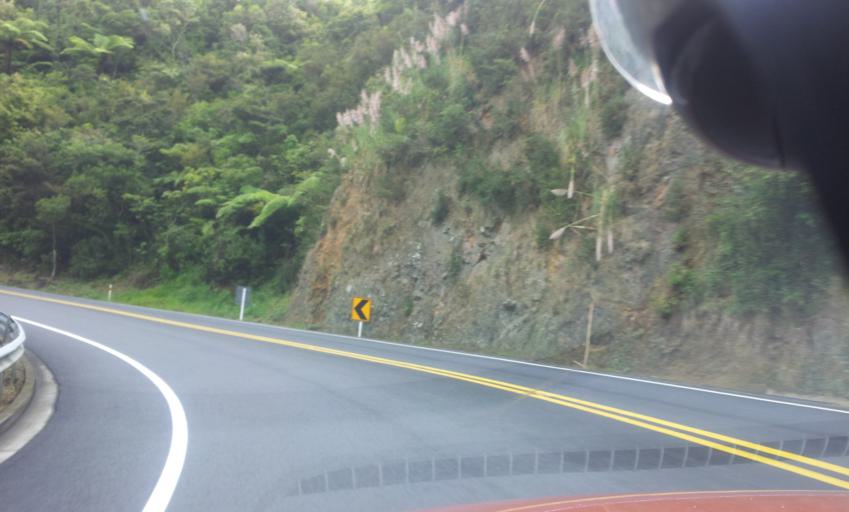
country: NZ
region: Northland
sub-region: Whangarei
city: Ruakaka
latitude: -36.0732
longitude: 174.4208
